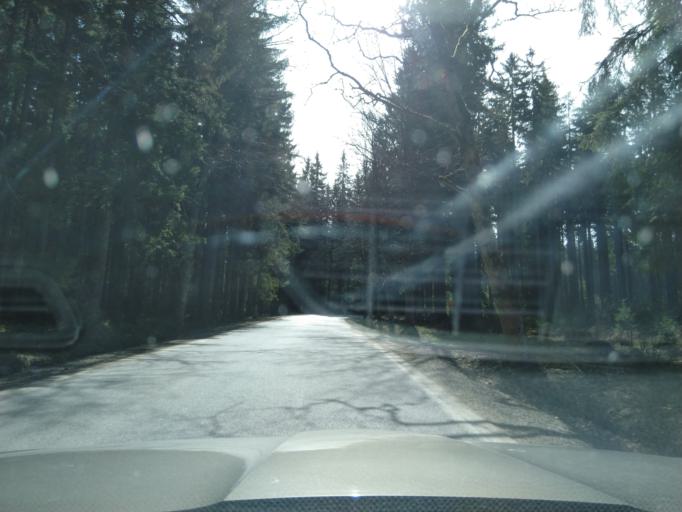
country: CZ
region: Jihocesky
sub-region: Okres Prachatice
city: Stachy
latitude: 49.0666
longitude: 13.6501
